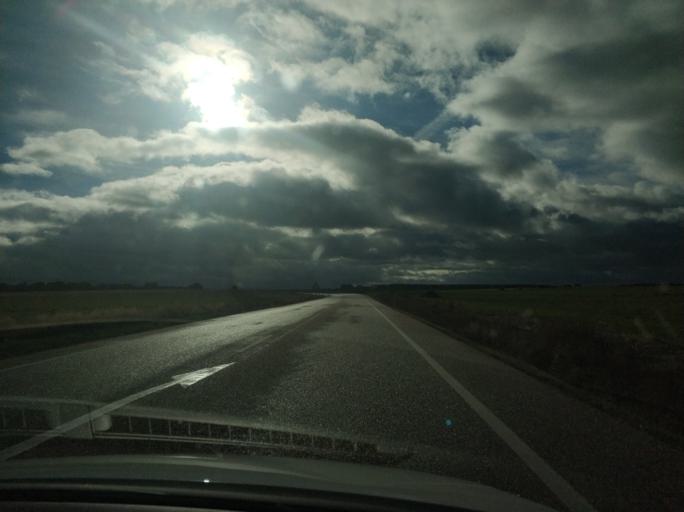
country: ES
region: Castille and Leon
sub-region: Provincia de Segovia
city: Corral de Ayllon
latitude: 41.3983
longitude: -3.4265
